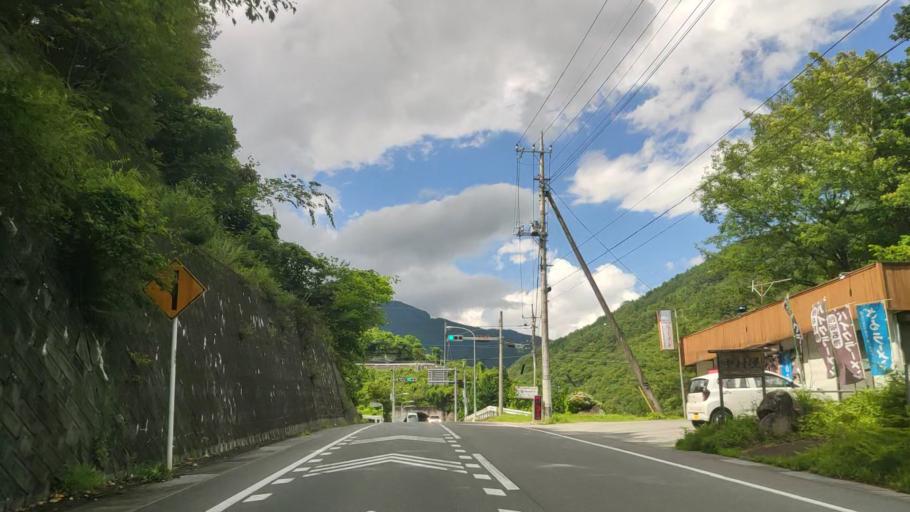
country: JP
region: Yamanashi
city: Enzan
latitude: 35.7772
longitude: 138.7387
